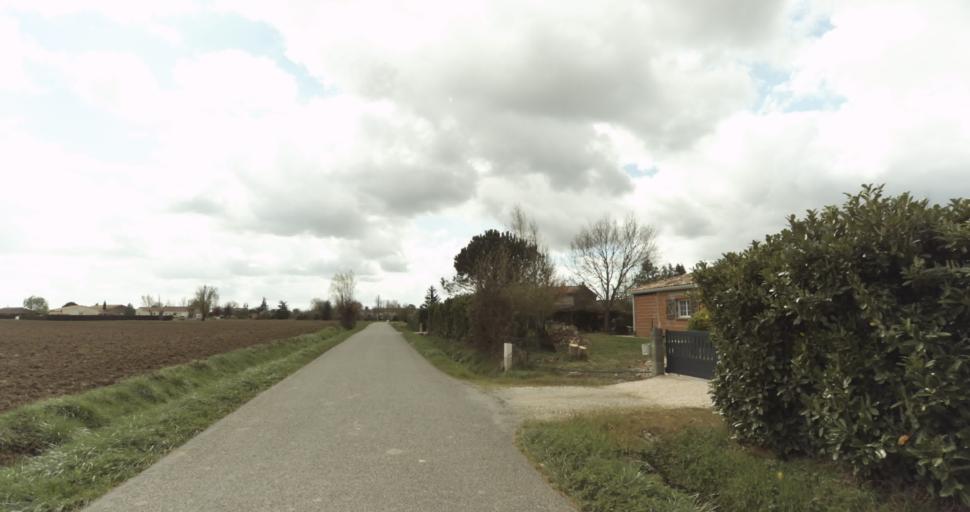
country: FR
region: Midi-Pyrenees
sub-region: Departement de la Haute-Garonne
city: Auterive
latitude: 43.3307
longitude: 1.4699
